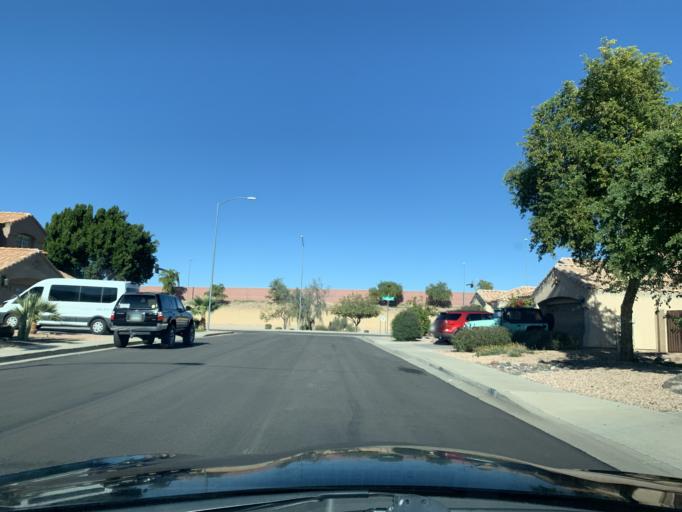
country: US
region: Arizona
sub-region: Pinal County
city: Apache Junction
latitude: 33.3852
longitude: -111.6202
